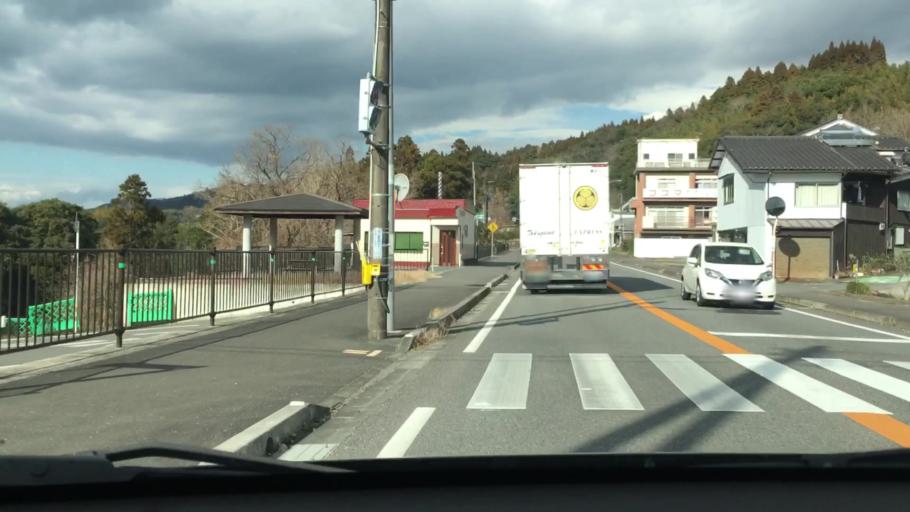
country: JP
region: Oita
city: Usuki
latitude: 33.0453
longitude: 131.6919
